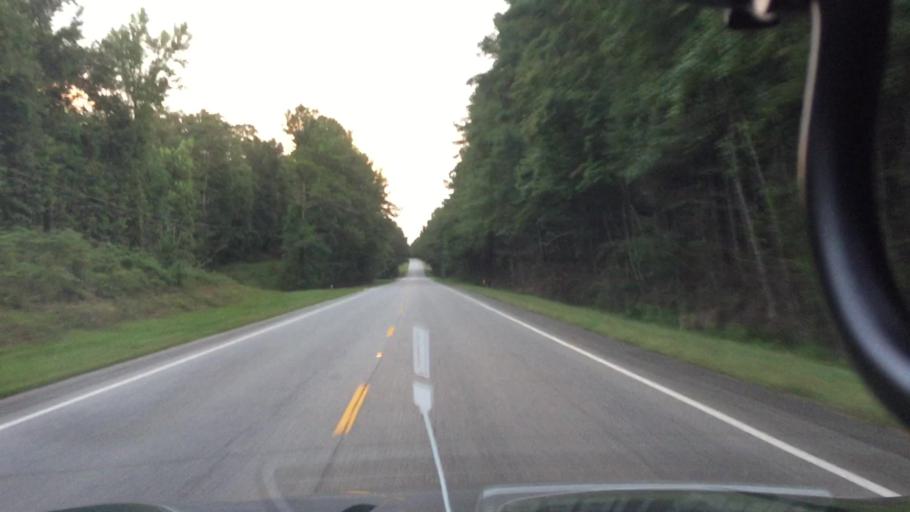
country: US
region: Alabama
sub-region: Coffee County
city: New Brockton
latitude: 31.4033
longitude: -85.8813
